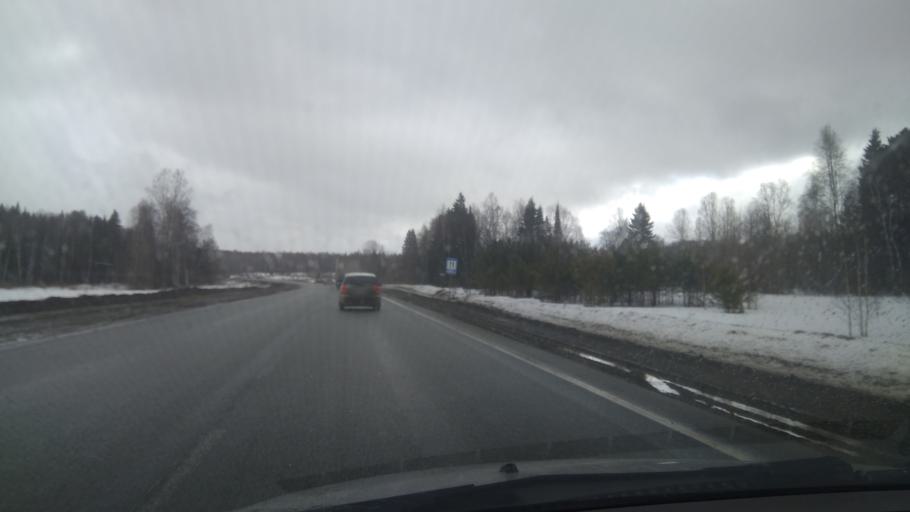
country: RU
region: Sverdlovsk
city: Ufimskiy
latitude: 56.7838
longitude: 58.3953
